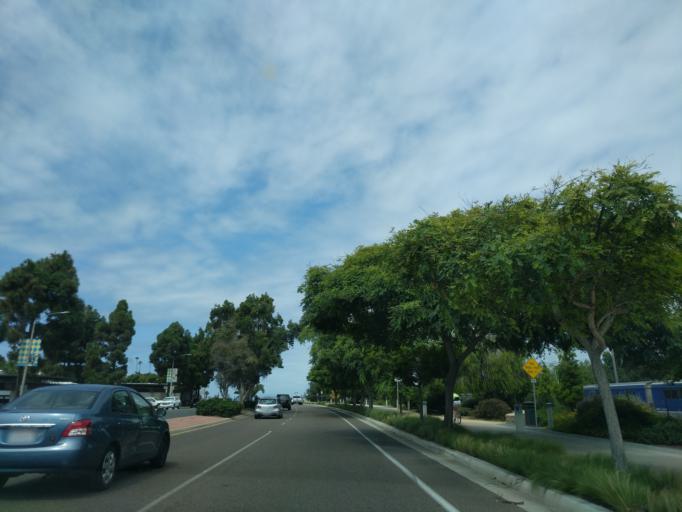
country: US
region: California
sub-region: San Diego County
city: Solana Beach
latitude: 32.9983
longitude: -117.2740
